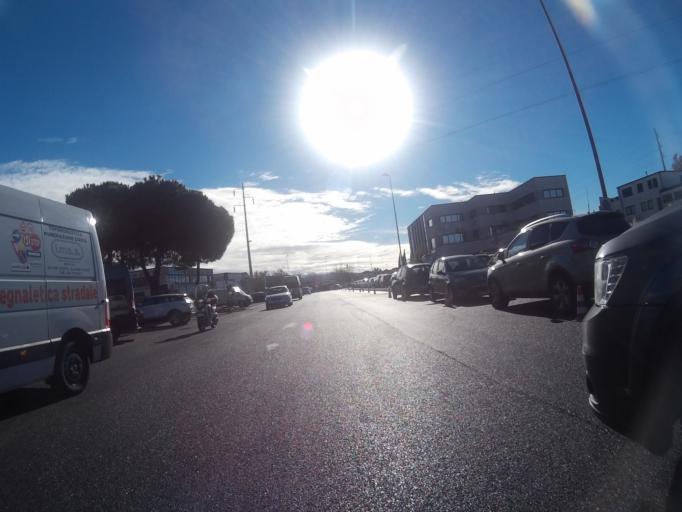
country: IT
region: Tuscany
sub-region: Provincia di Livorno
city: Livorno
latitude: 43.5671
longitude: 10.3415
